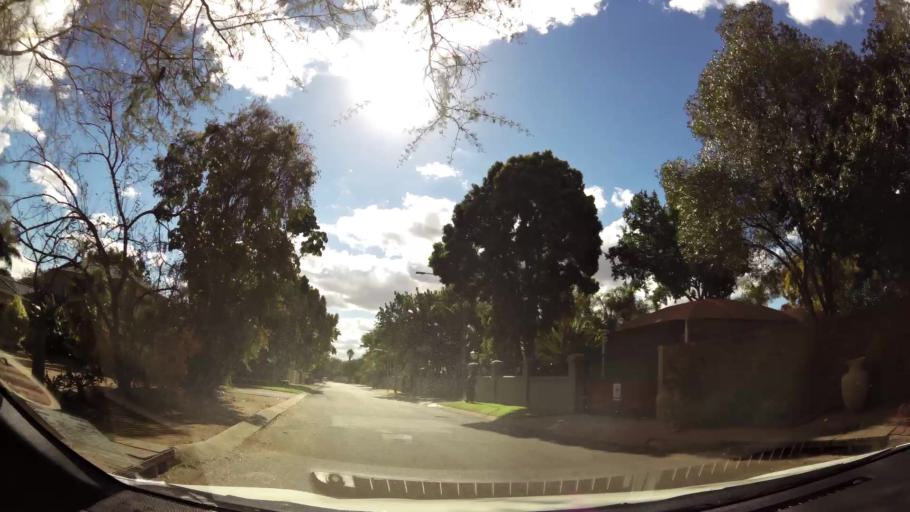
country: ZA
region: Limpopo
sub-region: Capricorn District Municipality
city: Polokwane
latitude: -23.8861
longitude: 29.4684
